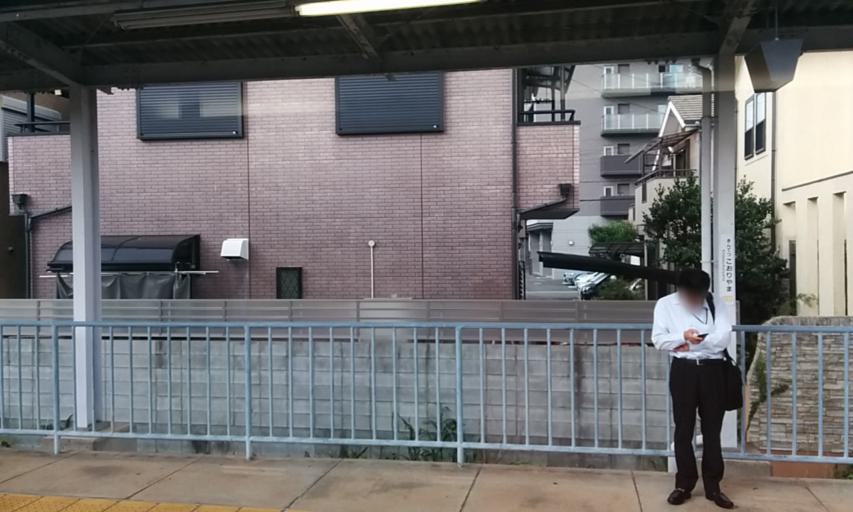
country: JP
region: Nara
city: Nara-shi
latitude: 34.6457
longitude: 135.7807
